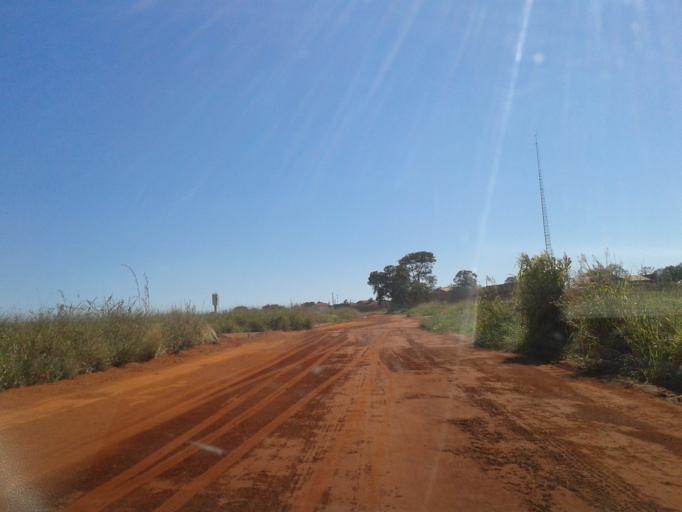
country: BR
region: Minas Gerais
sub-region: Santa Vitoria
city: Santa Vitoria
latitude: -18.8620
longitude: -50.1204
